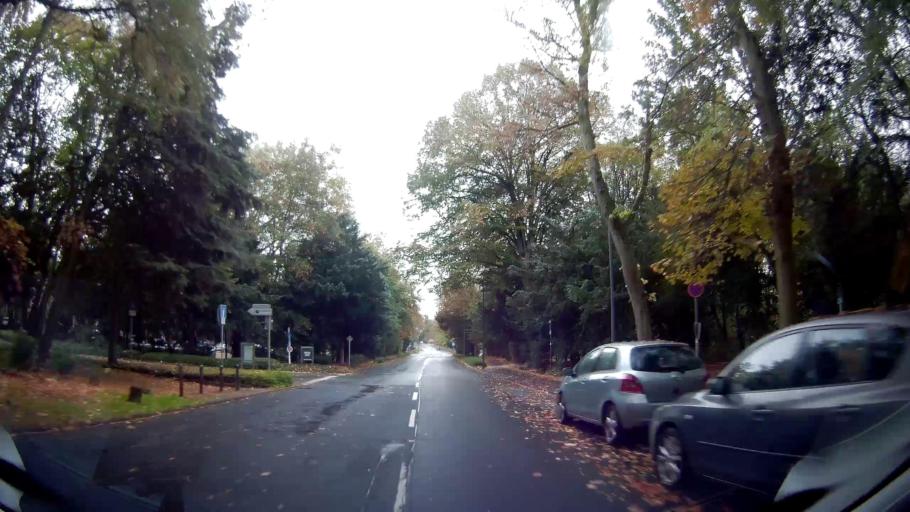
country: DE
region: North Rhine-Westphalia
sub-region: Regierungsbezirk Munster
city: Gladbeck
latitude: 51.5690
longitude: 7.0661
